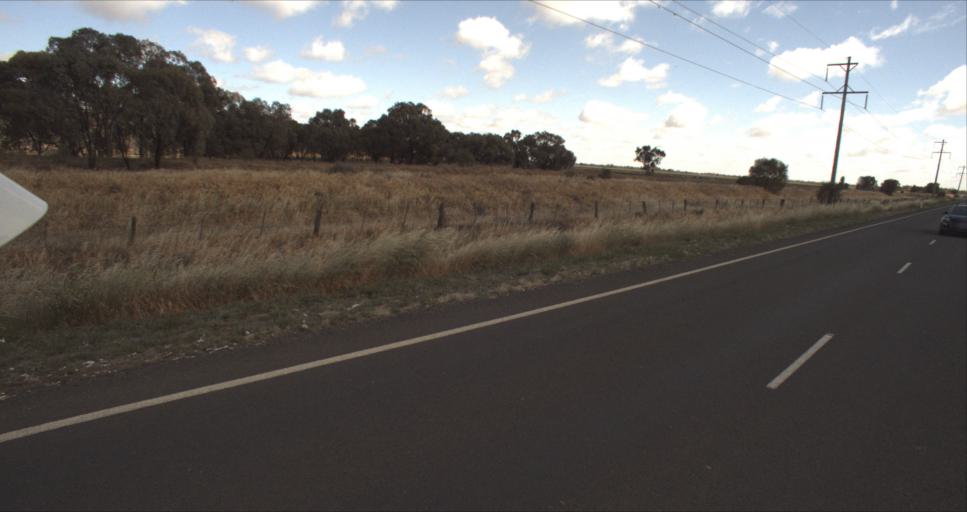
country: AU
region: New South Wales
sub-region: Murrumbidgee Shire
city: Darlington Point
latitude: -34.5436
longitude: 146.1717
